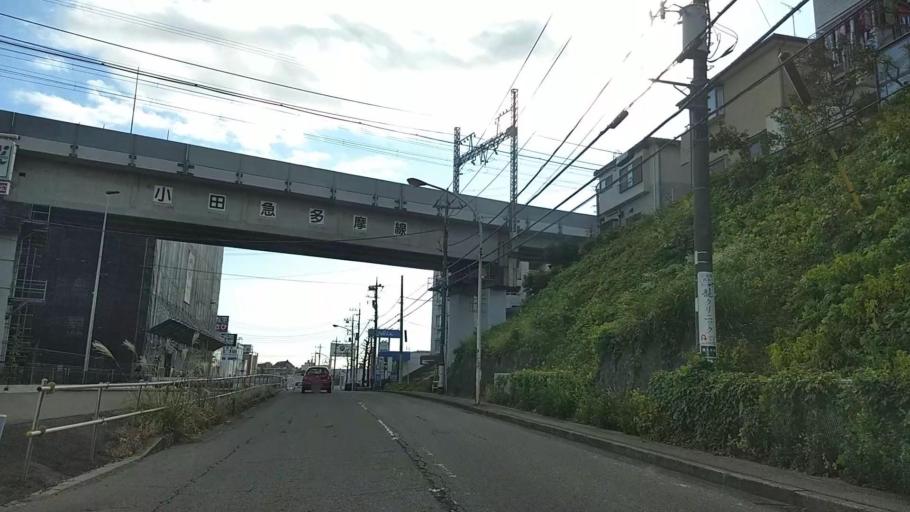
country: JP
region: Tokyo
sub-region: Machida-shi
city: Machida
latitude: 35.5994
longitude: 139.5000
